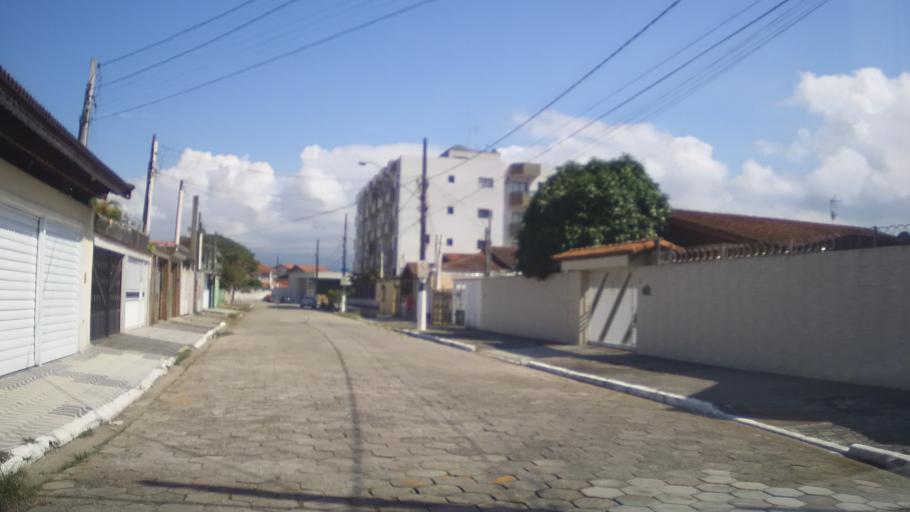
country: BR
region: Sao Paulo
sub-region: Praia Grande
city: Praia Grande
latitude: -24.0064
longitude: -46.4201
